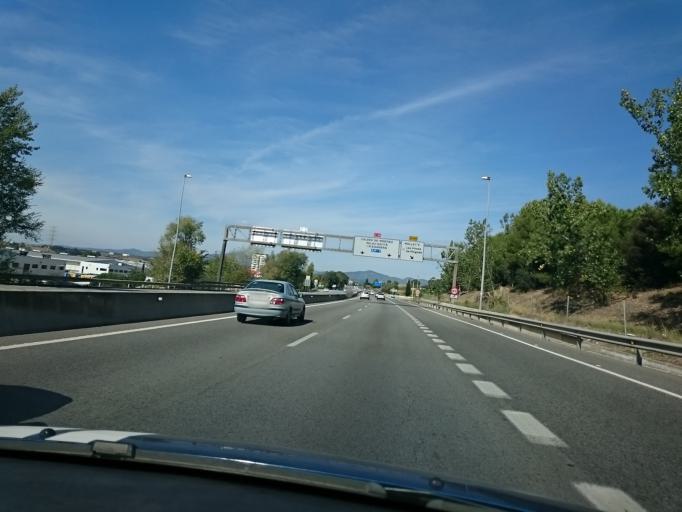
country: ES
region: Catalonia
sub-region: Provincia de Barcelona
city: Santa Perpetua de Mogoda
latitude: 41.5342
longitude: 2.1949
